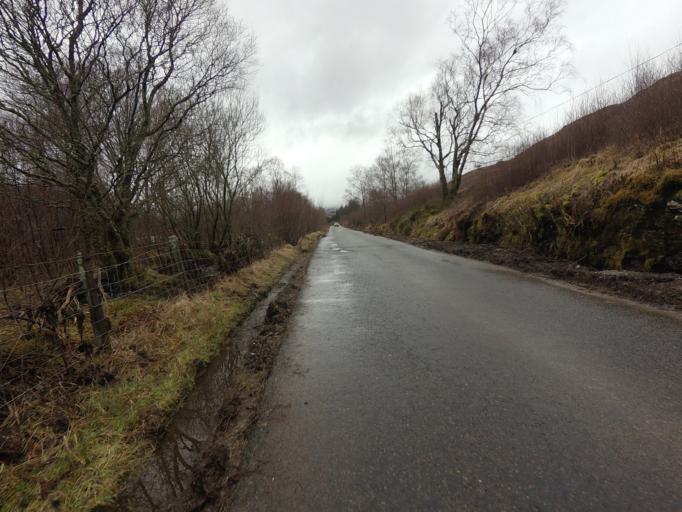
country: GB
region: Scotland
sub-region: West Dunbartonshire
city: Balloch
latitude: 56.2483
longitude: -4.6369
